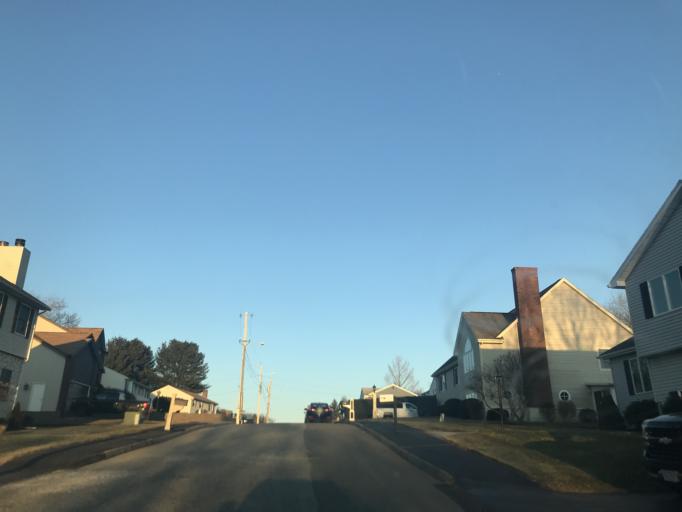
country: US
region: Massachusetts
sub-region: Essex County
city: Saugus
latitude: 42.4785
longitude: -71.0179
